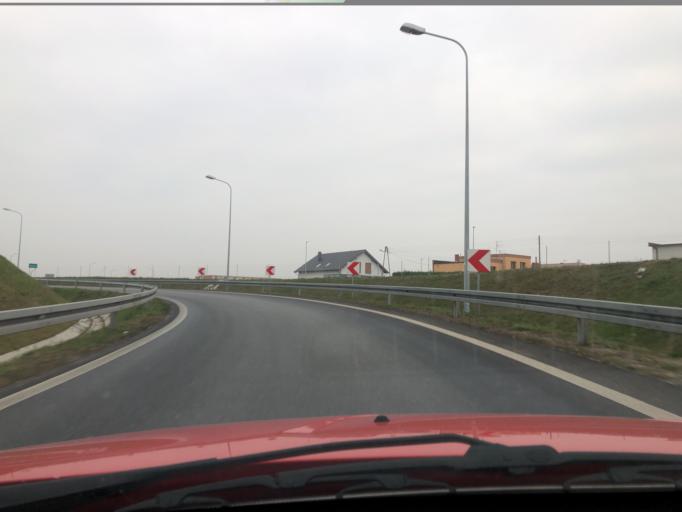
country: PL
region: Greater Poland Voivodeship
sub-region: Powiat jarocinski
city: Jarocin
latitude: 51.9781
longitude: 17.5220
